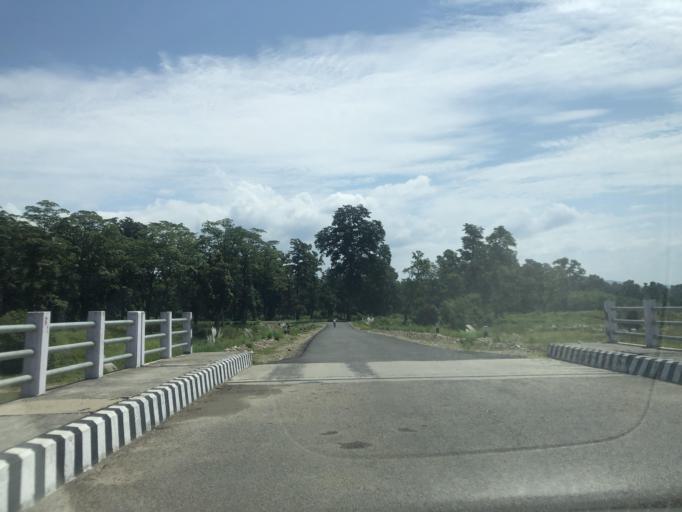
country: NP
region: Far Western
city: Tikapur
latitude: 28.5101
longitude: 81.3180
